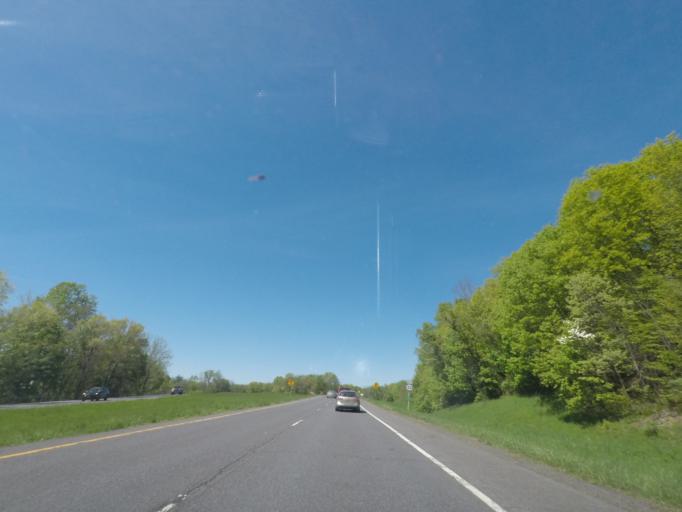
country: US
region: New York
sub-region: Ulster County
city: Lincoln Park
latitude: 41.9409
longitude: -73.9827
